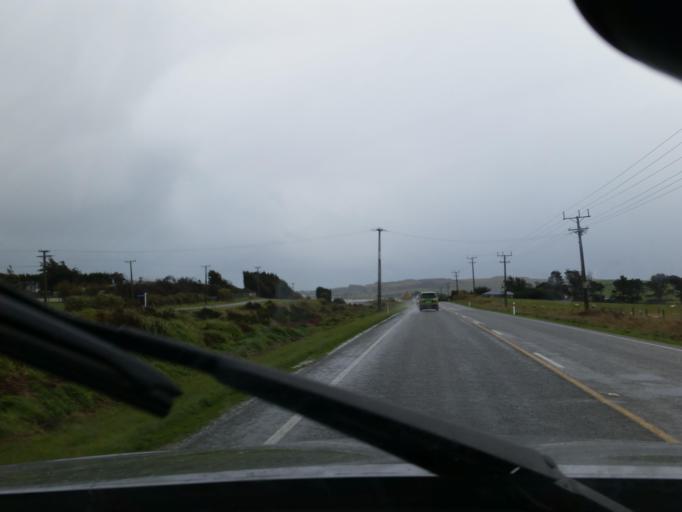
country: NZ
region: Southland
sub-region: Invercargill City
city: Bluff
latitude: -46.5425
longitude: 168.3016
